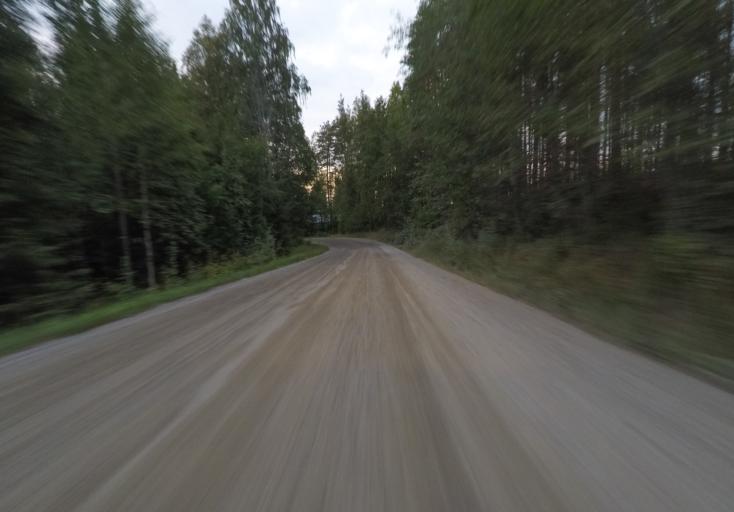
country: FI
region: Central Finland
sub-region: Jyvaeskylae
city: Hankasalmi
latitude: 62.4239
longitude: 26.6483
